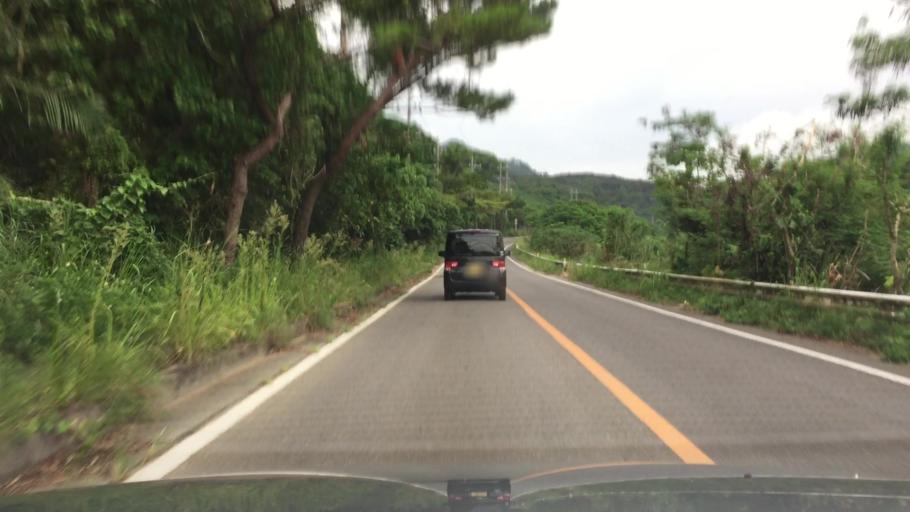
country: JP
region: Okinawa
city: Ishigaki
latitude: 24.3841
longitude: 124.1526
